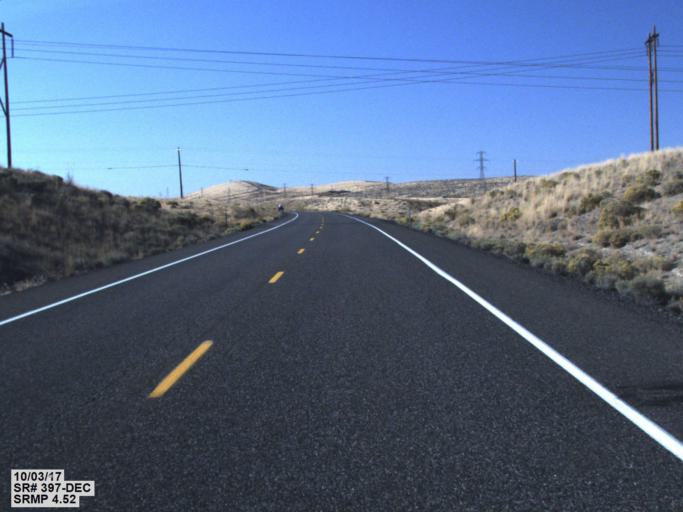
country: US
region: Washington
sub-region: Benton County
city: Highland
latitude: 46.1459
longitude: -119.1158
